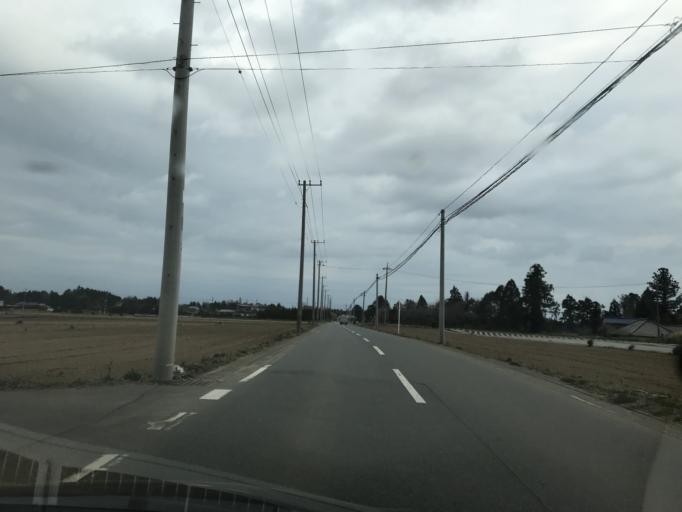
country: JP
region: Chiba
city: Sawara
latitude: 35.8371
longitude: 140.4951
